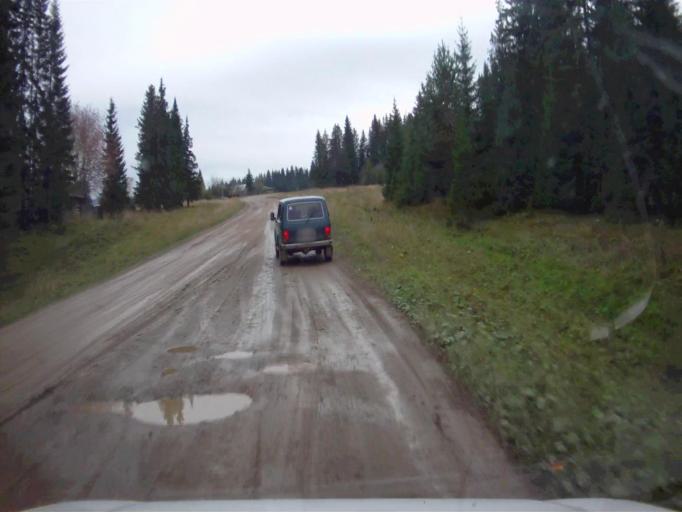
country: RU
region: Chelyabinsk
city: Nyazepetrovsk
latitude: 56.0630
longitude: 59.5659
